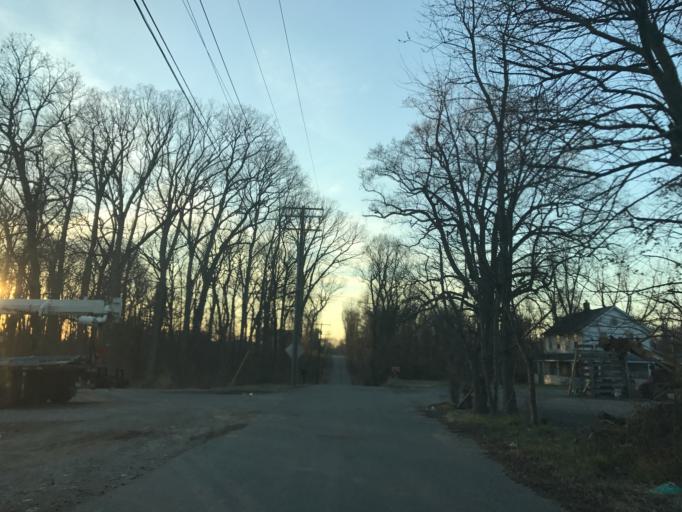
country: US
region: Maryland
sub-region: Baltimore County
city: White Marsh
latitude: 39.3616
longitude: -76.4479
